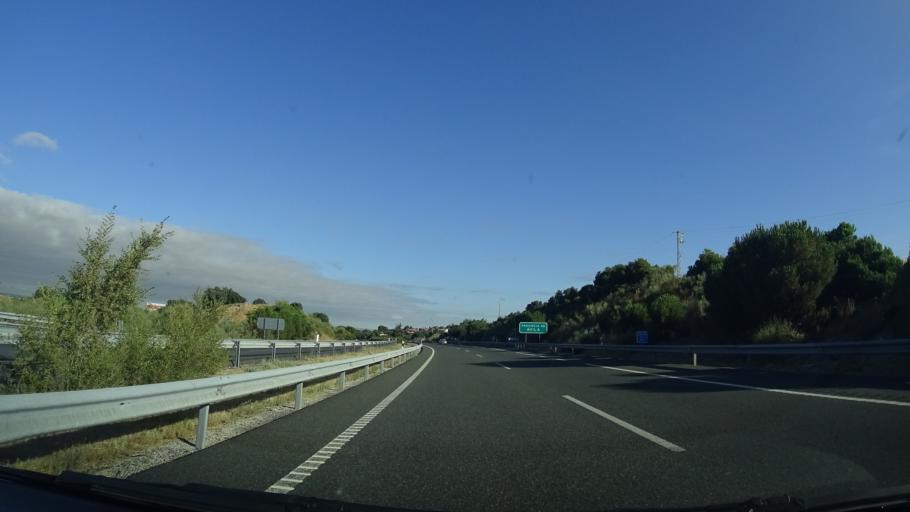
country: ES
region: Castille and Leon
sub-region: Provincia de Segovia
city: Labajos
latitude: 40.8529
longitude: -4.5455
